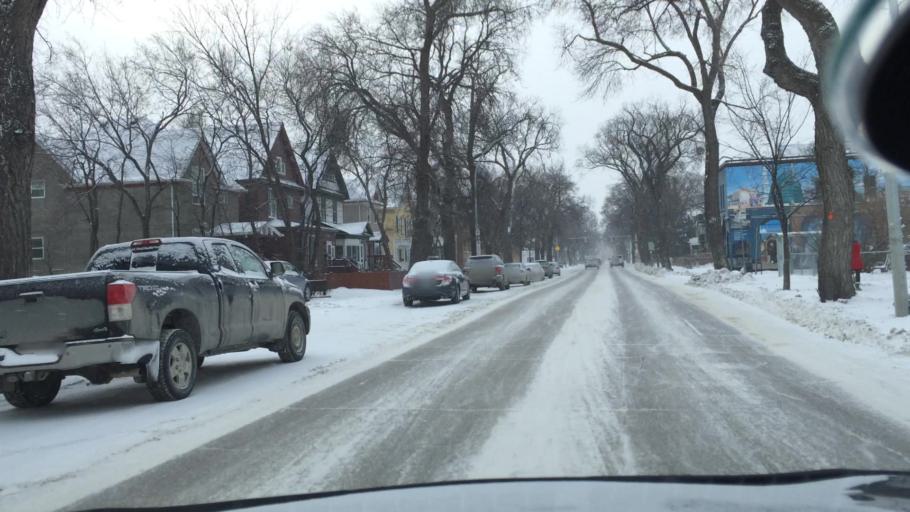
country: CA
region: Manitoba
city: Winnipeg
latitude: 49.8856
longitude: -97.1608
